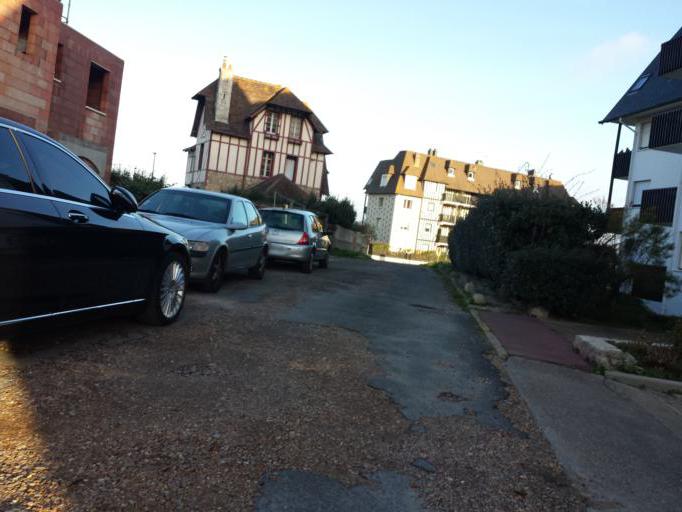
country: FR
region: Lower Normandy
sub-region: Departement du Calvados
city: Deauville
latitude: 49.3483
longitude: 0.0480
